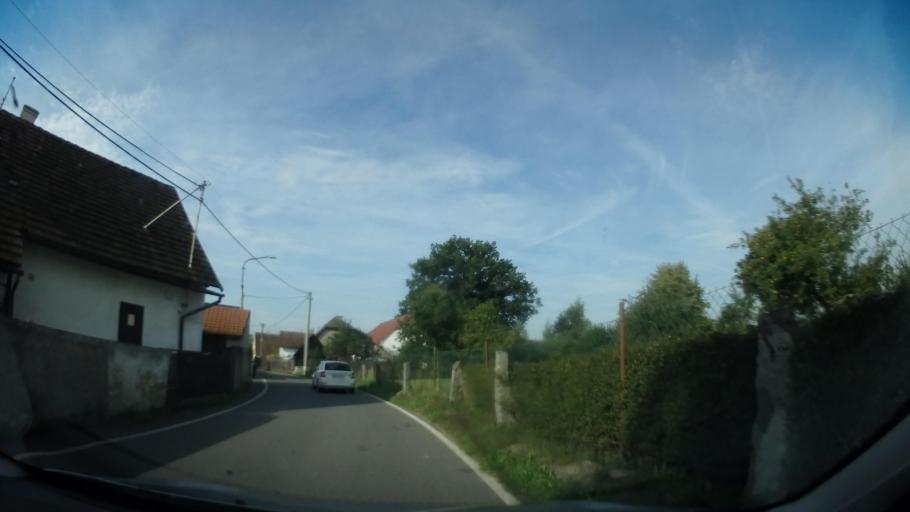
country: CZ
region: Jihocesky
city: Cimelice
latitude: 49.4261
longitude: 14.1207
